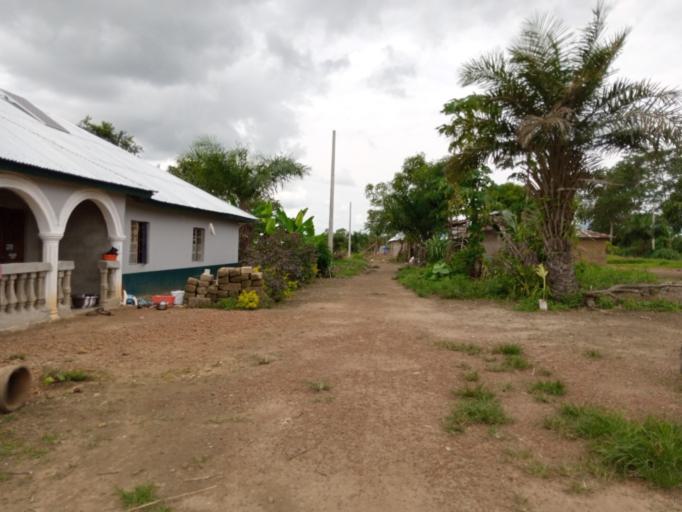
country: SL
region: Southern Province
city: Moyamba
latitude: 8.1662
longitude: -12.4195
